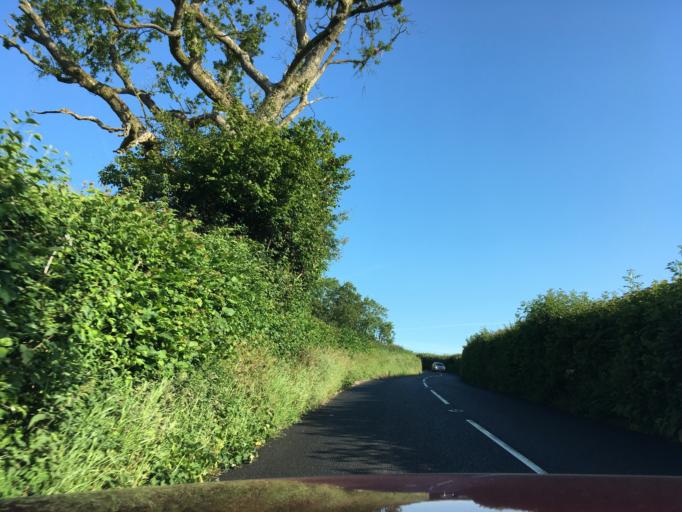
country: GB
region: Wales
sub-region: Monmouthshire
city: Tintern
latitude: 51.7255
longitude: -2.6362
